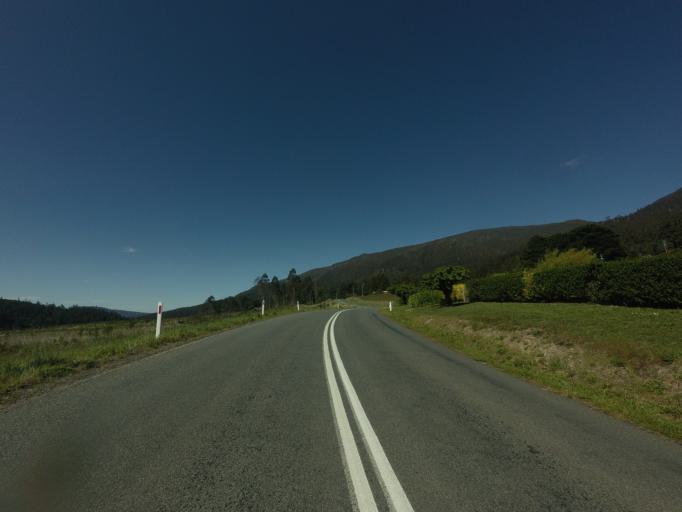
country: AU
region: Tasmania
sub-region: Derwent Valley
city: New Norfolk
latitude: -42.7514
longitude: 146.6369
